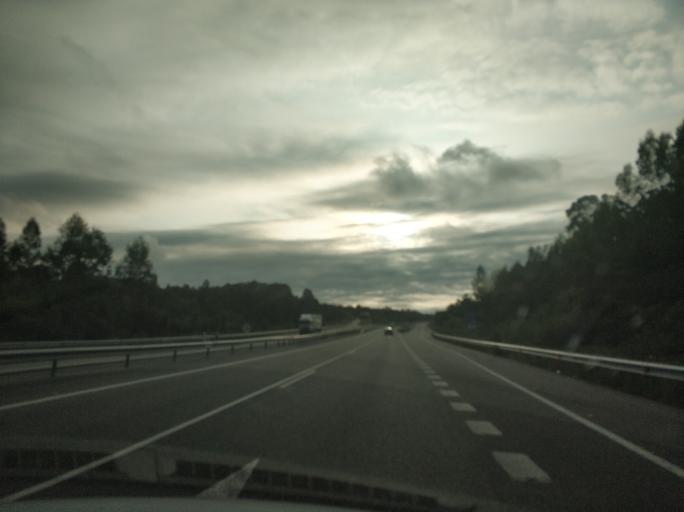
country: ES
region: Asturias
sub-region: Province of Asturias
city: Cudillero
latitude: 43.5561
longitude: -6.2001
